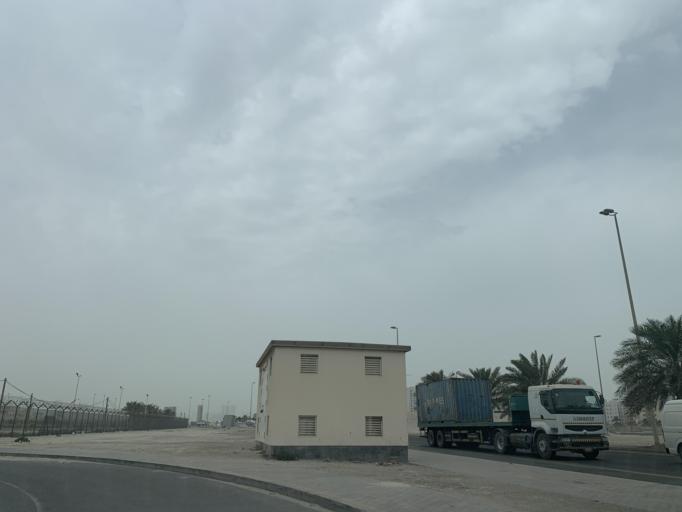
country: BH
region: Muharraq
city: Al Hadd
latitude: 26.2258
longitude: 50.6616
